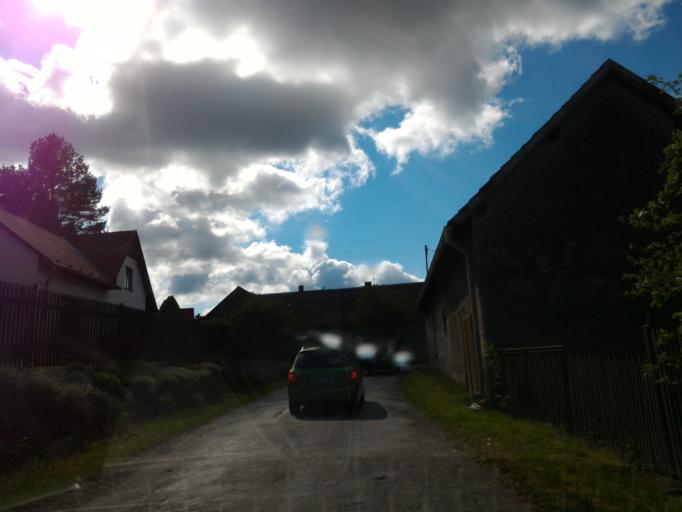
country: CZ
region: Vysocina
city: Ledec nad Sazavou
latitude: 49.6247
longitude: 15.3100
